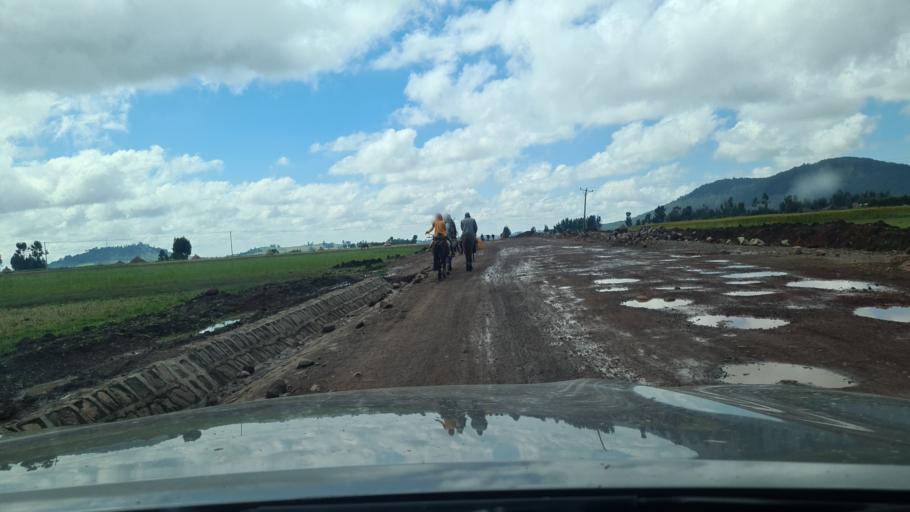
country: ET
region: Oromiya
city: Huruta
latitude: 8.0929
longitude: 39.5366
